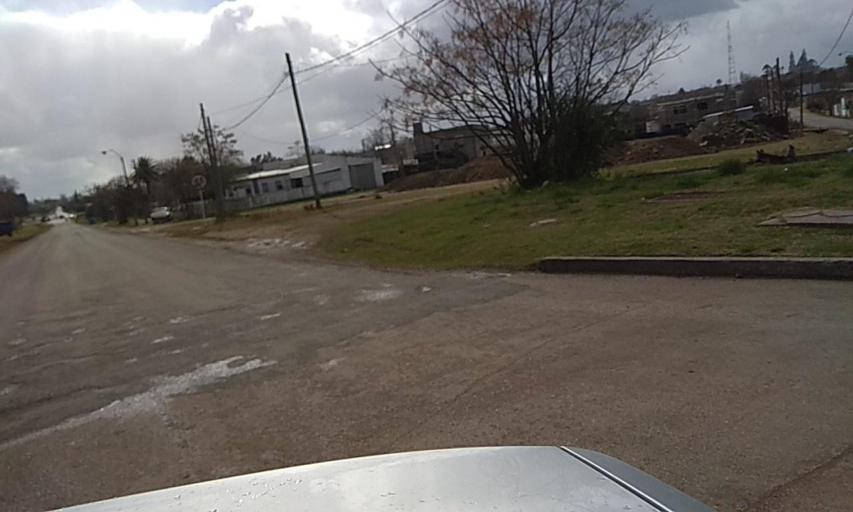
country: UY
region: Florida
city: Florida
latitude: -34.1080
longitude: -56.2235
